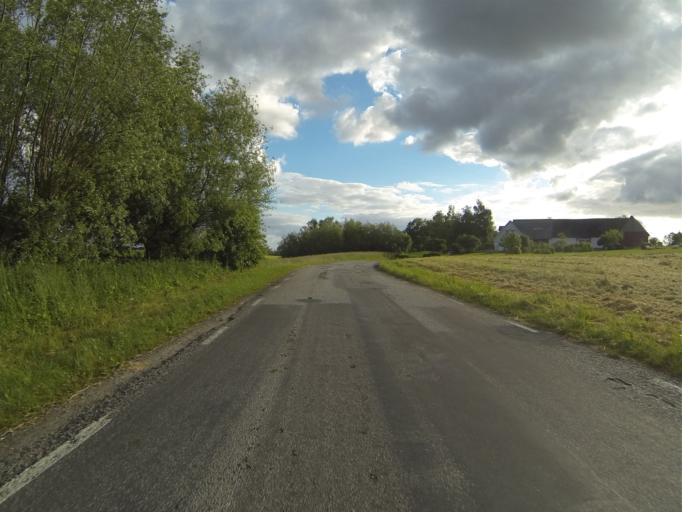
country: SE
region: Skane
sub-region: Staffanstorps Kommun
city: Staffanstorp
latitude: 55.6715
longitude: 13.2398
